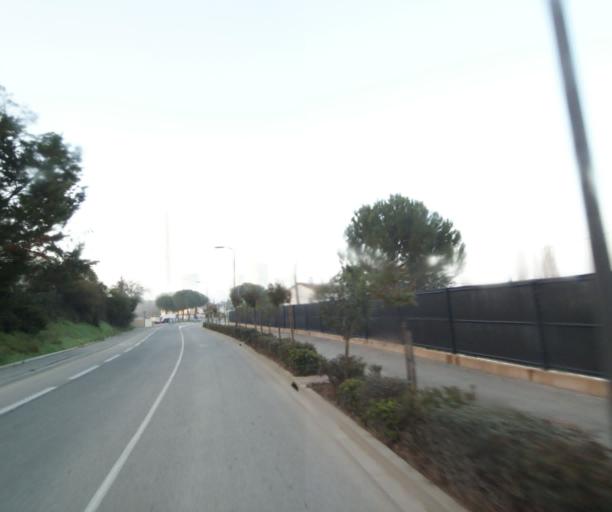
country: FR
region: Provence-Alpes-Cote d'Azur
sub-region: Departement des Bouches-du-Rhone
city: Meyreuil
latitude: 43.4789
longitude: 5.4926
